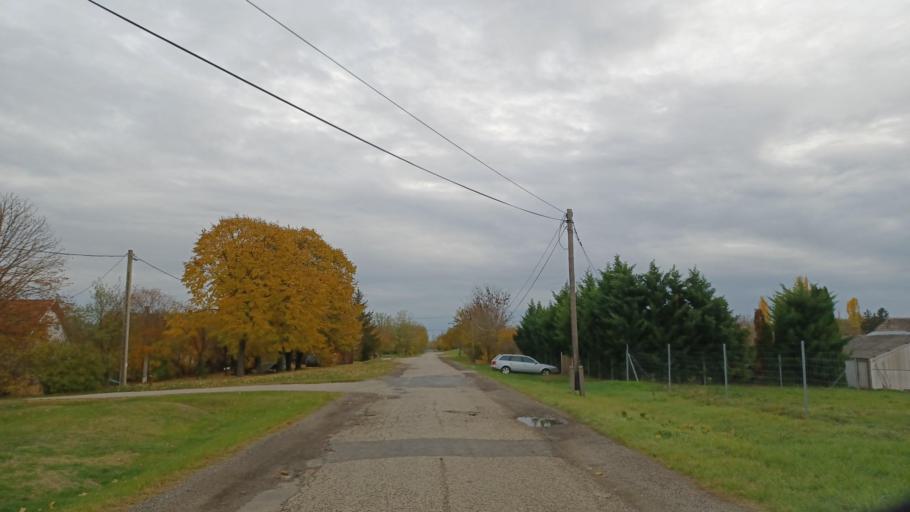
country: HU
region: Tolna
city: Simontornya
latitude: 46.6885
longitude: 18.5950
